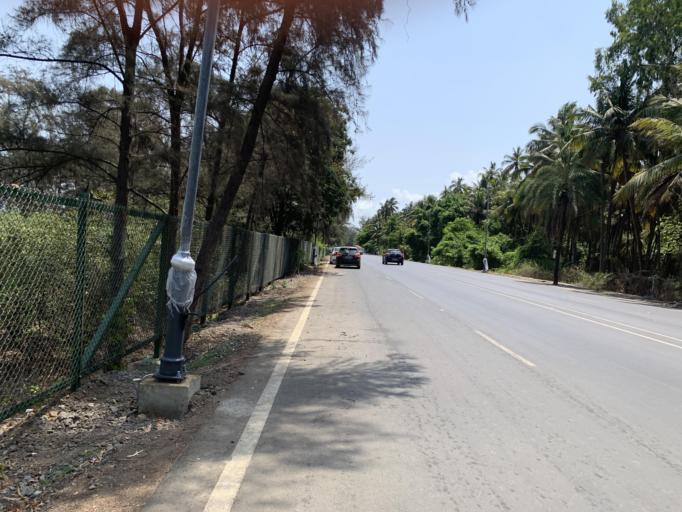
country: IN
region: Daman and Diu
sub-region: Daman District
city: Daman
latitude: 20.4608
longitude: 72.8480
